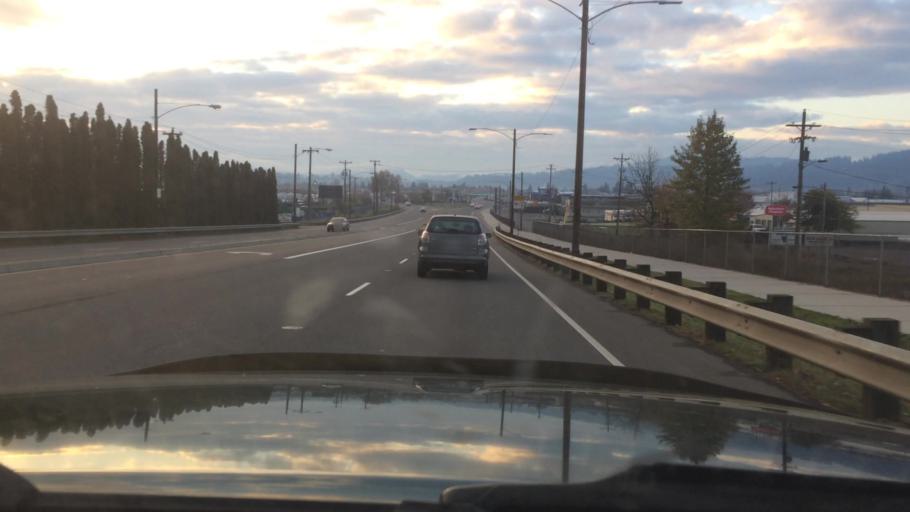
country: US
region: Oregon
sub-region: Lane County
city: Eugene
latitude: 44.0585
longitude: -123.1321
